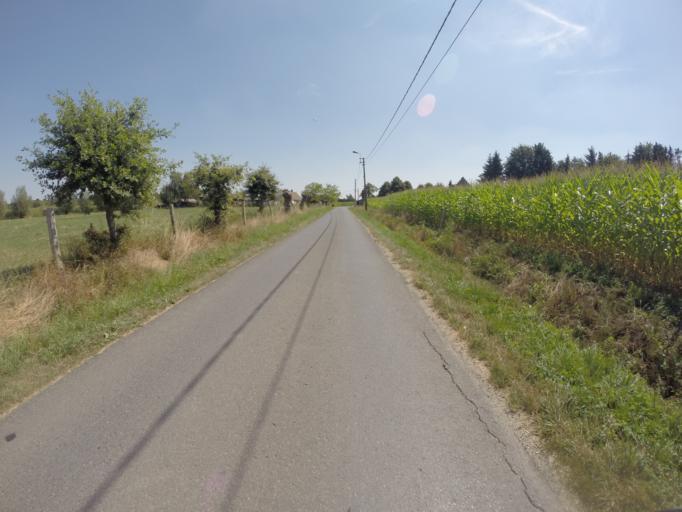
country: BE
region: Flanders
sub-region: Provincie Oost-Vlaanderen
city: Knesselare
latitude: 51.1440
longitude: 3.4380
